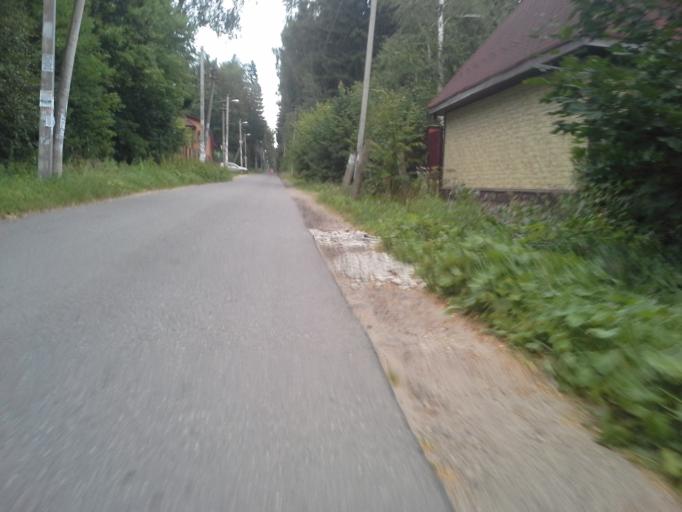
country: RU
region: Moskovskaya
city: Zhavoronki
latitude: 55.6330
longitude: 37.0713
